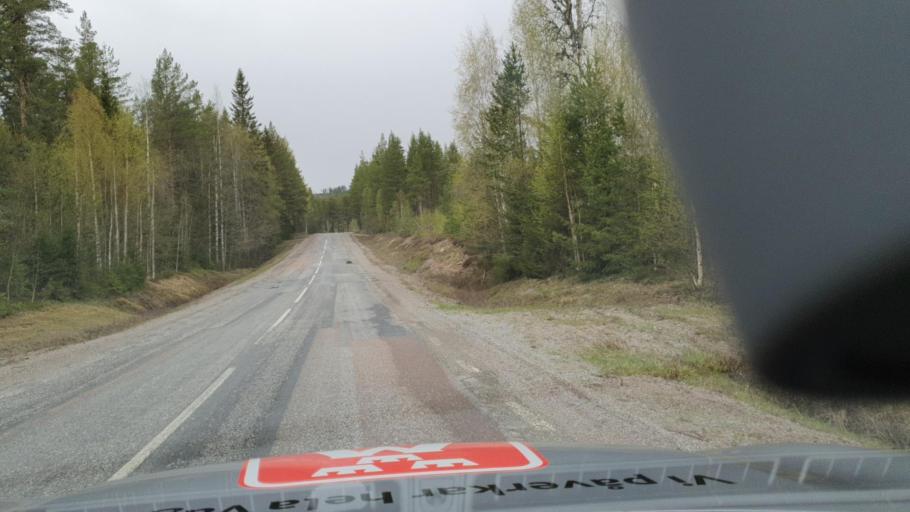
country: SE
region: Vaesterbotten
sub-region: Asele Kommun
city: Asele
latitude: 63.6920
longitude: 17.2338
